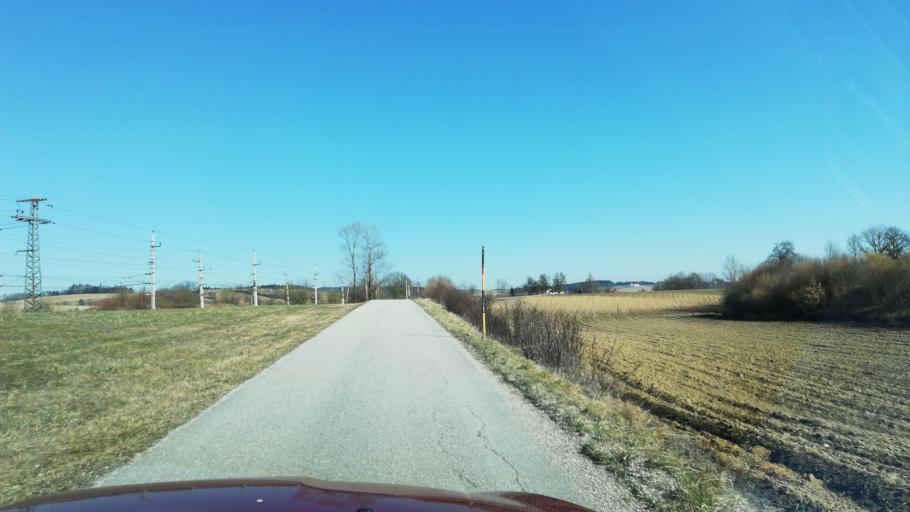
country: AT
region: Upper Austria
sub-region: Politischer Bezirk Vocklabruck
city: Schlatt
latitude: 48.0816
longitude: 13.8058
